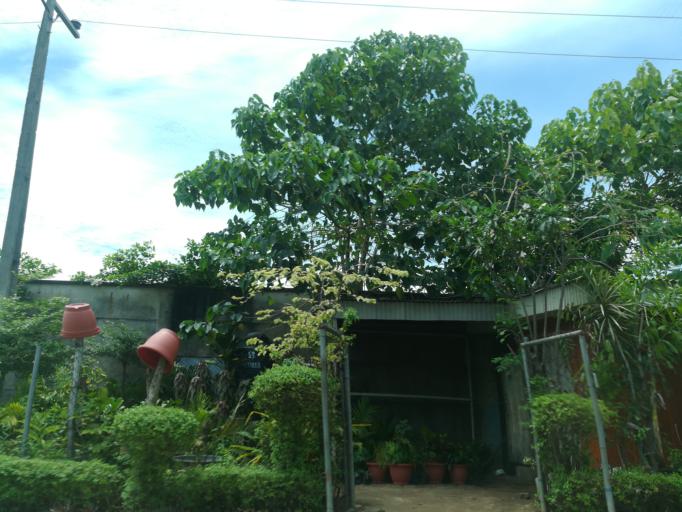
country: NG
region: Lagos
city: Ebute Ikorodu
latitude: 6.5736
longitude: 3.4856
